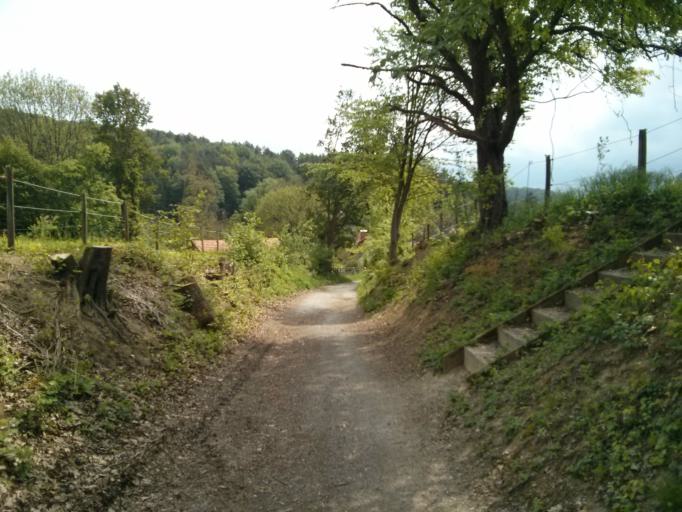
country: AT
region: Styria
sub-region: Politischer Bezirk Graz-Umgebung
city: Stattegg
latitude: 47.1352
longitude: 15.4241
